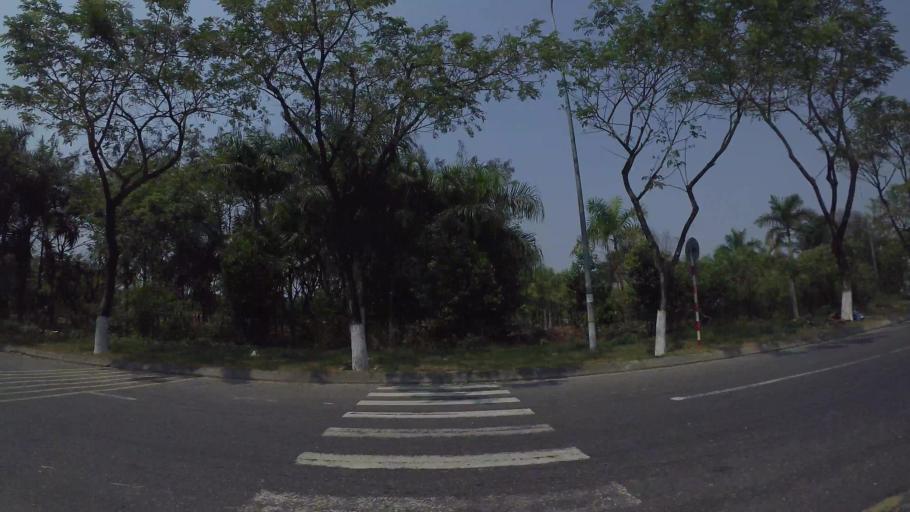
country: VN
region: Da Nang
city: Cam Le
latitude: 16.0132
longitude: 108.1953
